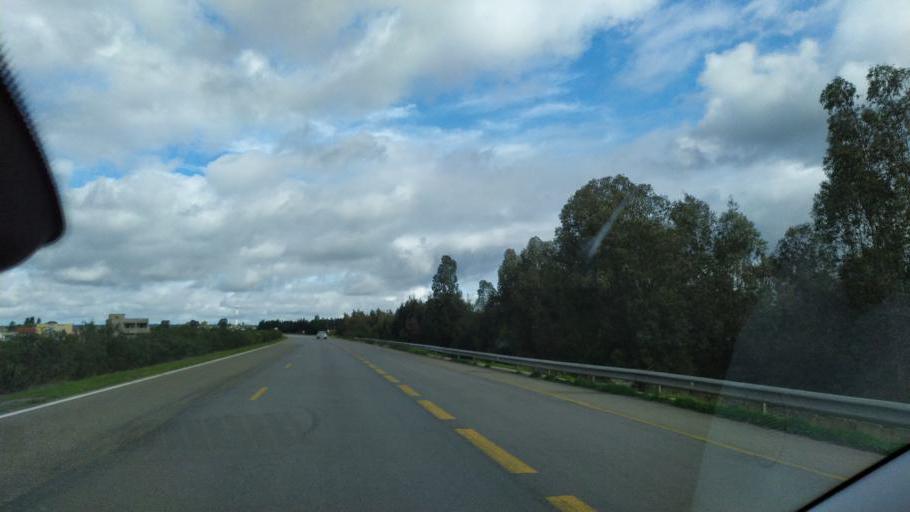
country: MA
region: Gharb-Chrarda-Beni Hssen
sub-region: Kenitra Province
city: Lalla Mimouna
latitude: 34.8782
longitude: -6.2124
